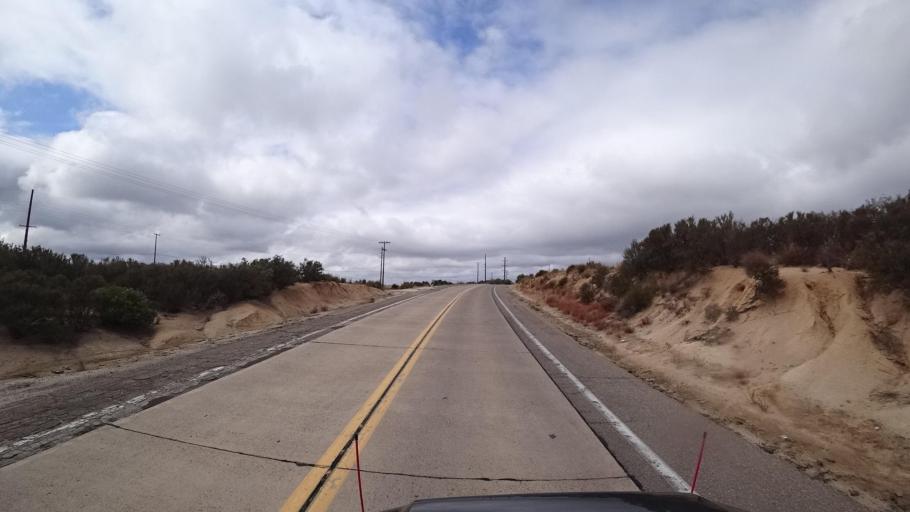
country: US
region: California
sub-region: San Diego County
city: Campo
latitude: 32.6969
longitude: -116.3504
